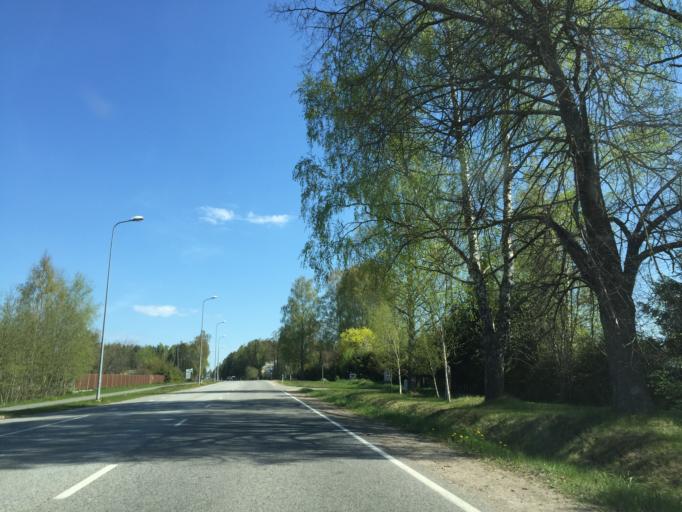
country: LV
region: Saulkrastu
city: Saulkrasti
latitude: 57.3201
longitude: 24.4233
